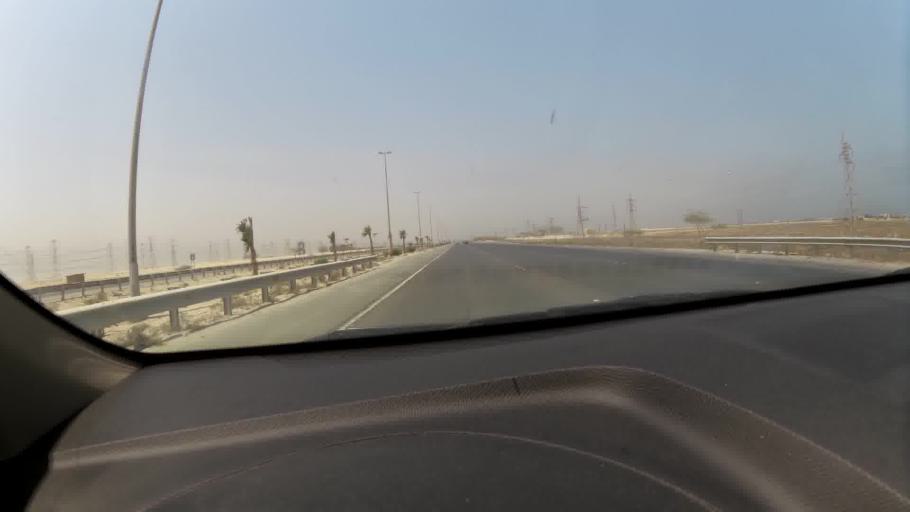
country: KW
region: Al Ahmadi
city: Al Fahahil
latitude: 28.8031
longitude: 48.2692
